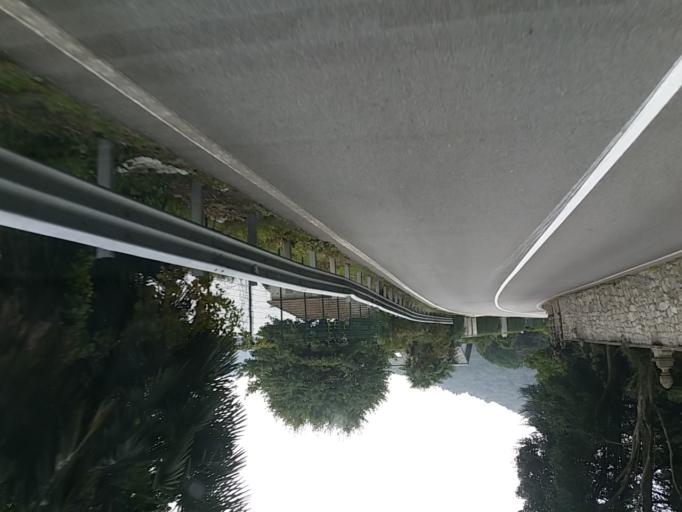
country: IT
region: Piedmont
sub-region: Provincia di Novara
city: Ameno
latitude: 45.7804
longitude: 8.4261
